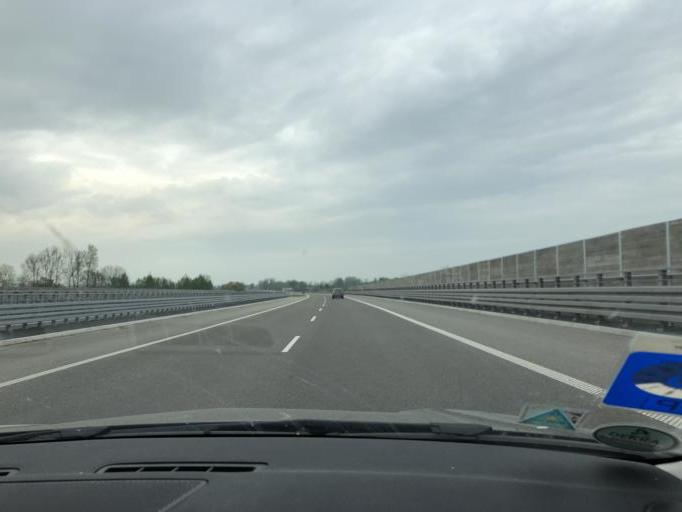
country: PL
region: Subcarpathian Voivodeship
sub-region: Powiat lancucki
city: Bialobrzegi
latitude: 50.1150
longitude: 22.3148
